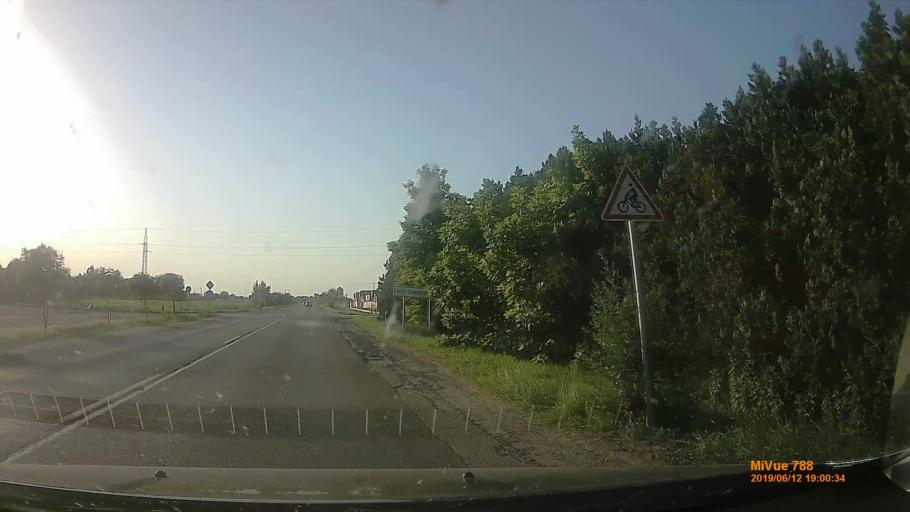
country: HU
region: Bacs-Kiskun
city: Kiskunfelegyhaza
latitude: 46.7301
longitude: 19.8451
